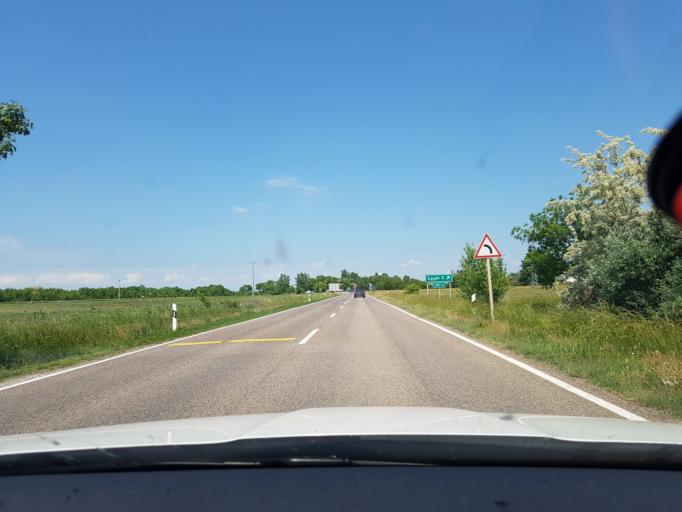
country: HU
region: Hajdu-Bihar
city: Egyek
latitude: 47.5876
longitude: 20.8531
